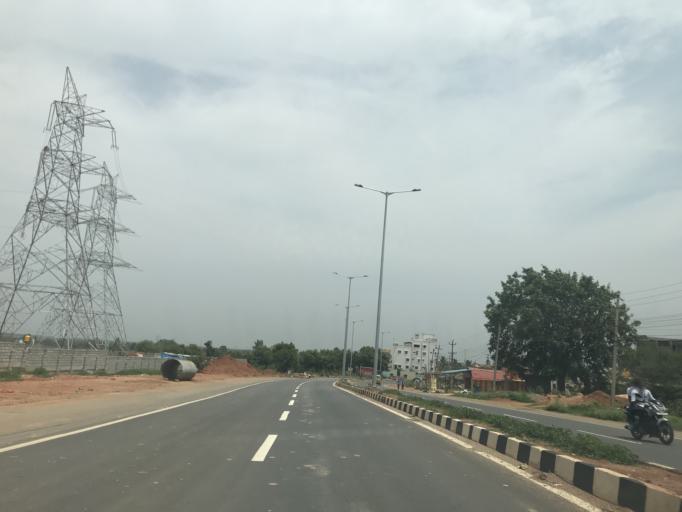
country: IN
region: Karnataka
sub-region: Bangalore Urban
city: Yelahanka
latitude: 13.1451
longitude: 77.6733
